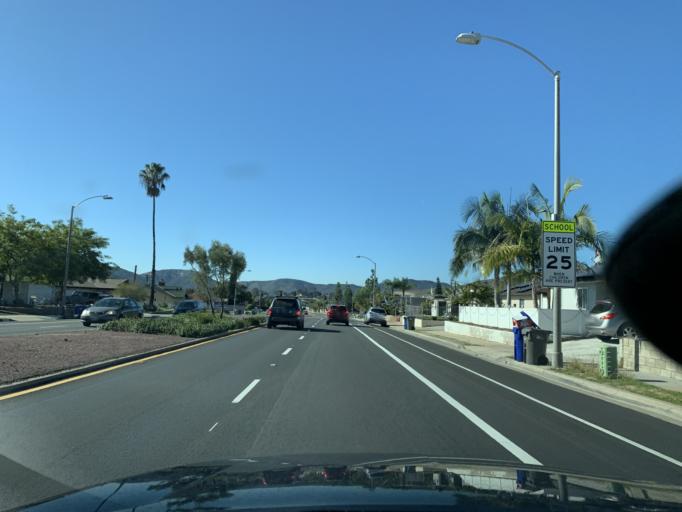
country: US
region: California
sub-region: San Diego County
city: Santee
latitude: 32.8524
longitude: -116.9968
